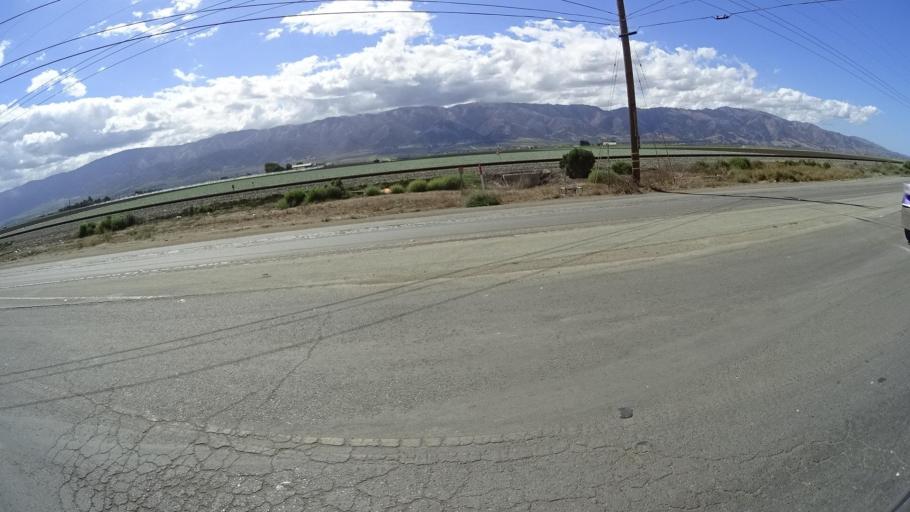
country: US
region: California
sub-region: Monterey County
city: Gonzales
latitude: 36.5298
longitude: -121.4608
